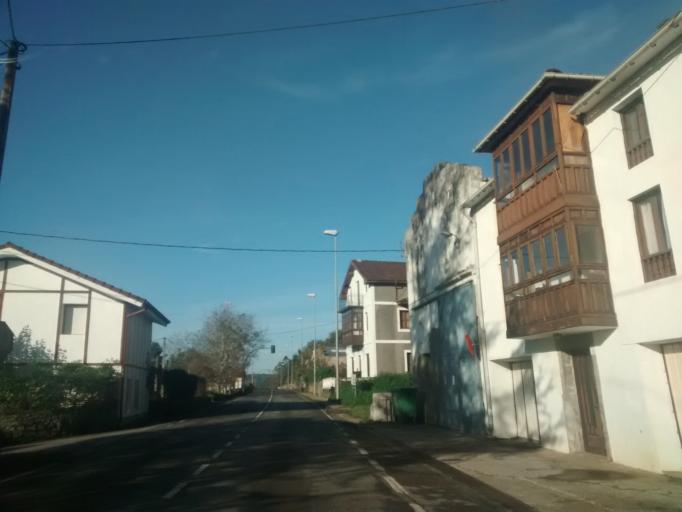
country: ES
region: Cantabria
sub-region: Provincia de Cantabria
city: Entrambasaguas
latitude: 43.3436
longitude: -3.6758
